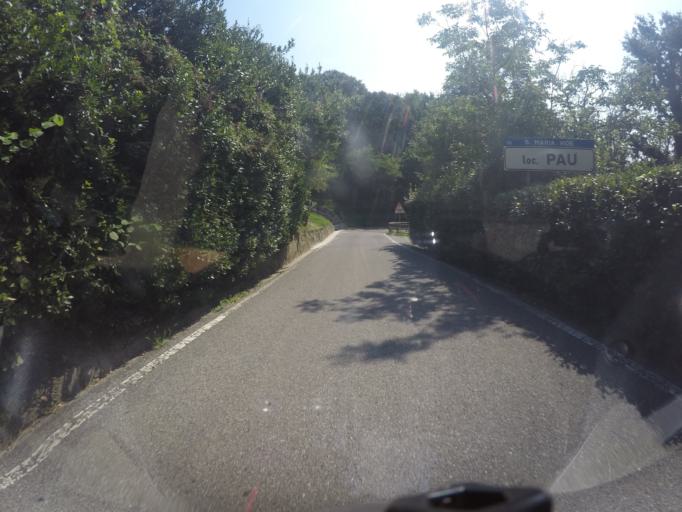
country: IT
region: Lombardy
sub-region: Provincia di Lecco
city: Santa Maria Hoe
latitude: 45.7481
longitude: 9.3868
